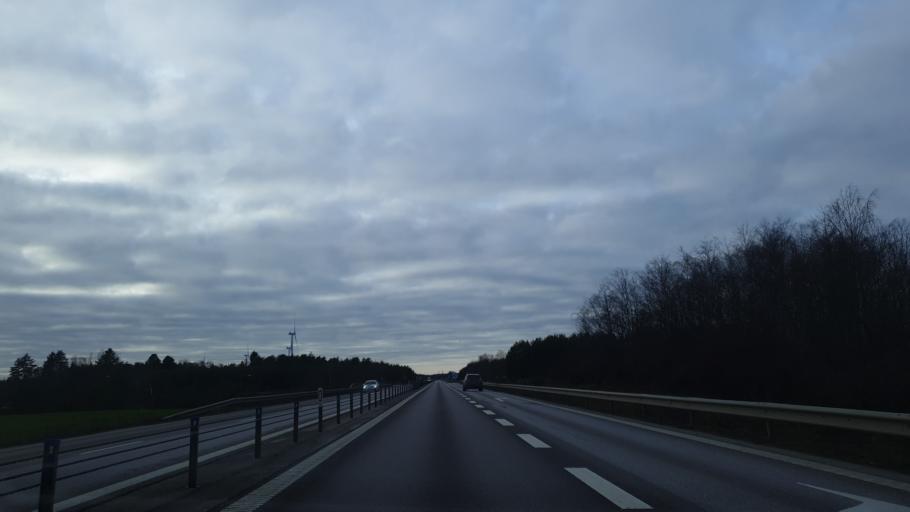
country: SE
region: Kalmar
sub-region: Kalmar Kommun
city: Ljungbyholm
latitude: 56.6235
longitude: 16.1731
